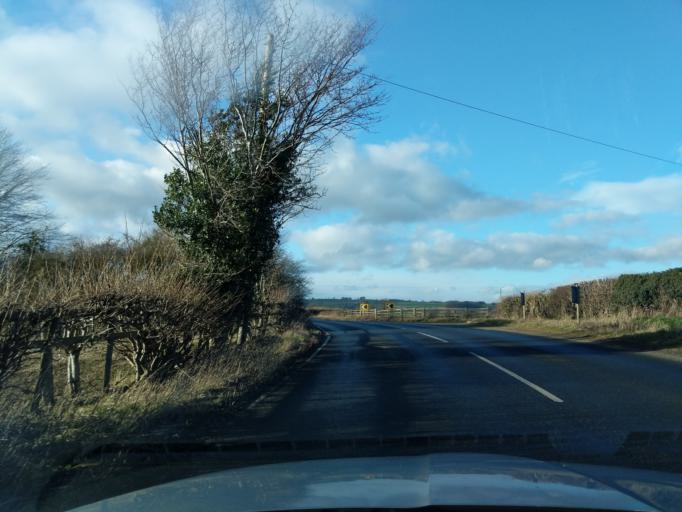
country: GB
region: England
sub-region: North Yorkshire
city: Catterick
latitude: 54.3176
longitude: -1.6759
